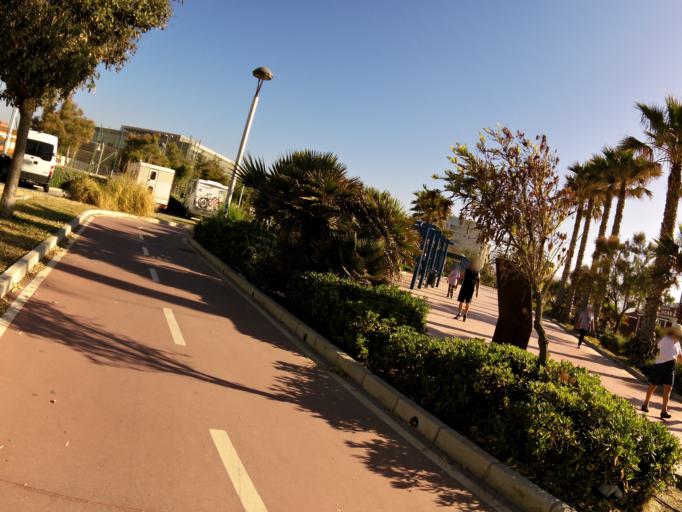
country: ES
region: Andalusia
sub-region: Provincia de Malaga
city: Malaga
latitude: 36.6877
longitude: -4.4435
